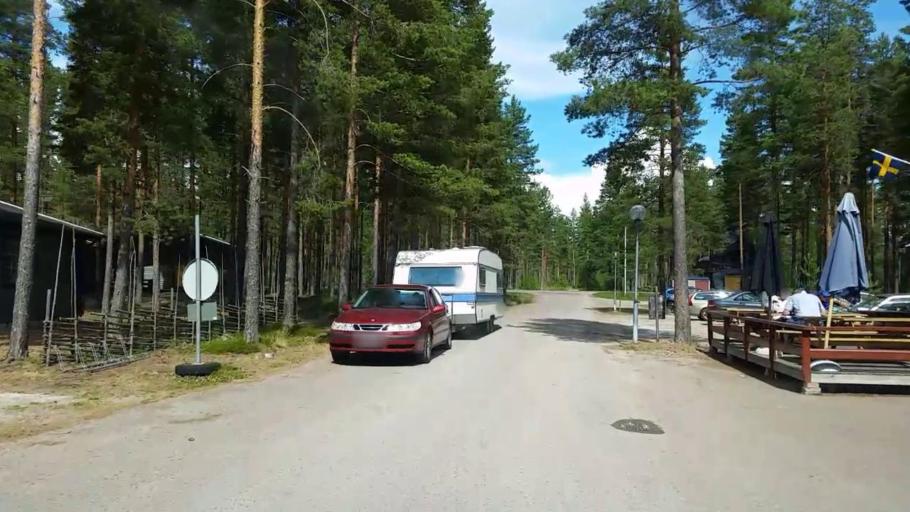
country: SE
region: Dalarna
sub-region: Rattviks Kommun
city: Raettvik
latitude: 61.1727
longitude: 15.1657
